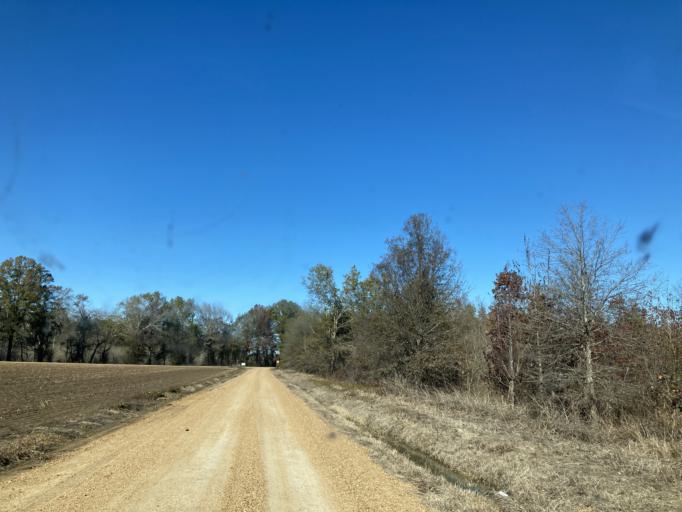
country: US
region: Mississippi
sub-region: Sharkey County
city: Rolling Fork
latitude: 32.7538
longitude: -90.6901
